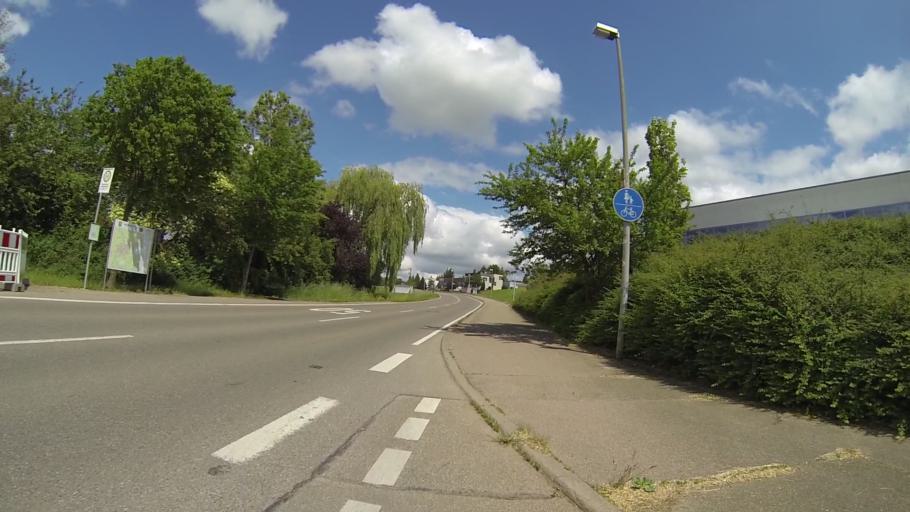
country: DE
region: Baden-Wuerttemberg
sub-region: Regierungsbezirk Stuttgart
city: Waldstetten
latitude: 48.7714
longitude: 9.8307
